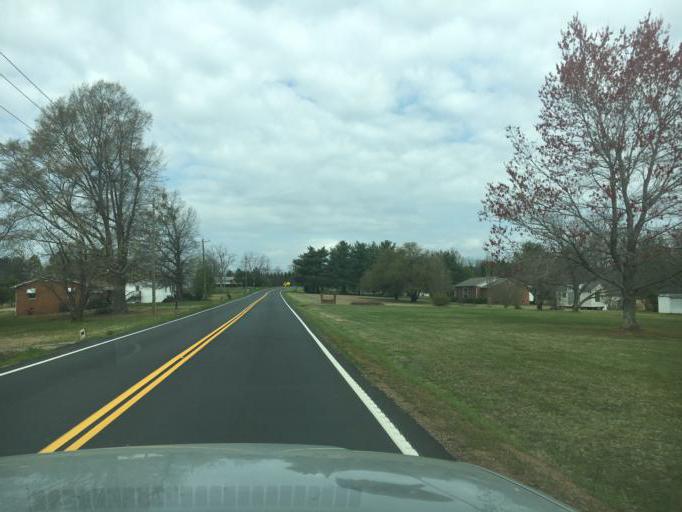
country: US
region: South Carolina
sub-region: Spartanburg County
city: Inman Mills
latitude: 35.0720
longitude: -82.1784
